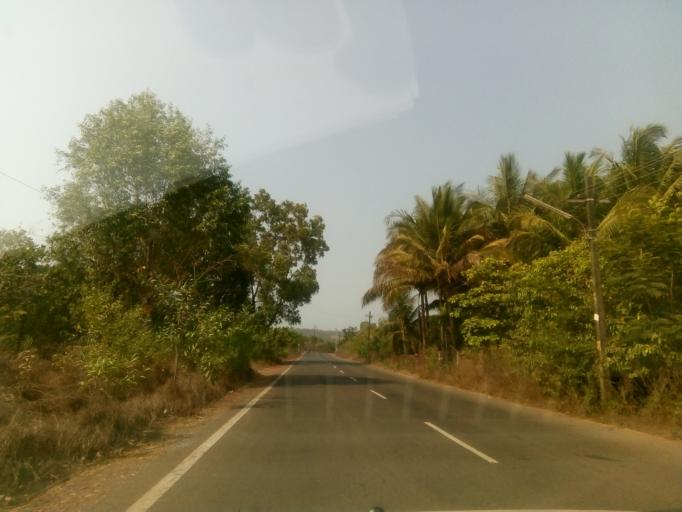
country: IN
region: Goa
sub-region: North Goa
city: Pernem
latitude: 15.6898
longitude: 73.8403
